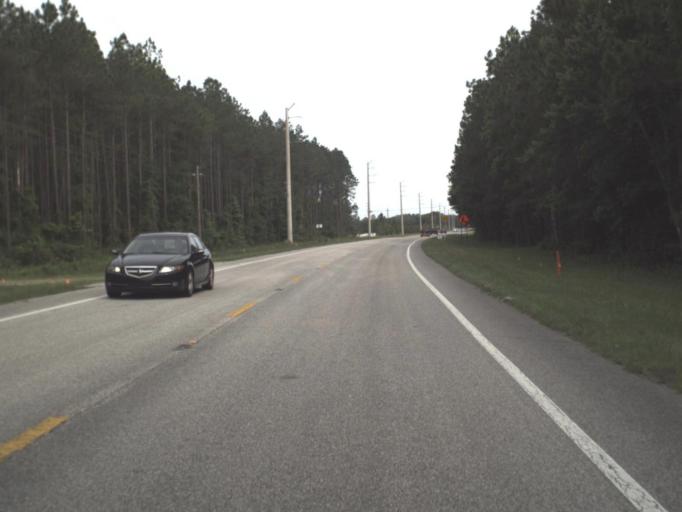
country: US
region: Florida
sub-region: Saint Johns County
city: Saint Augustine
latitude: 29.9351
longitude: -81.4340
